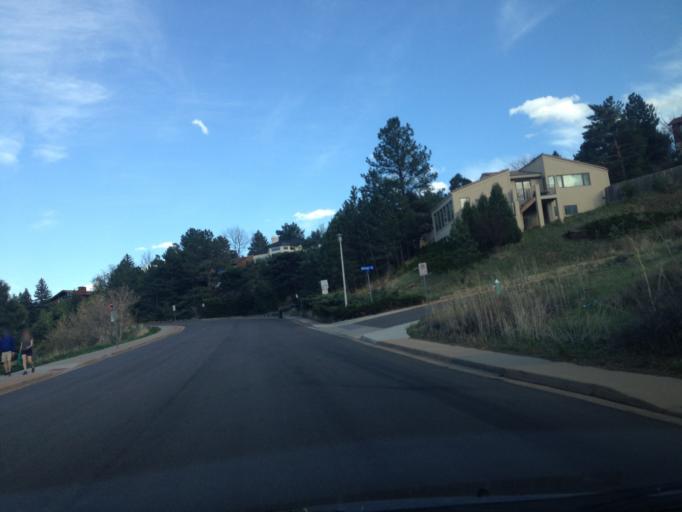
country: US
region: Colorado
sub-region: Boulder County
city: Boulder
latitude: 39.9705
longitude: -105.2504
